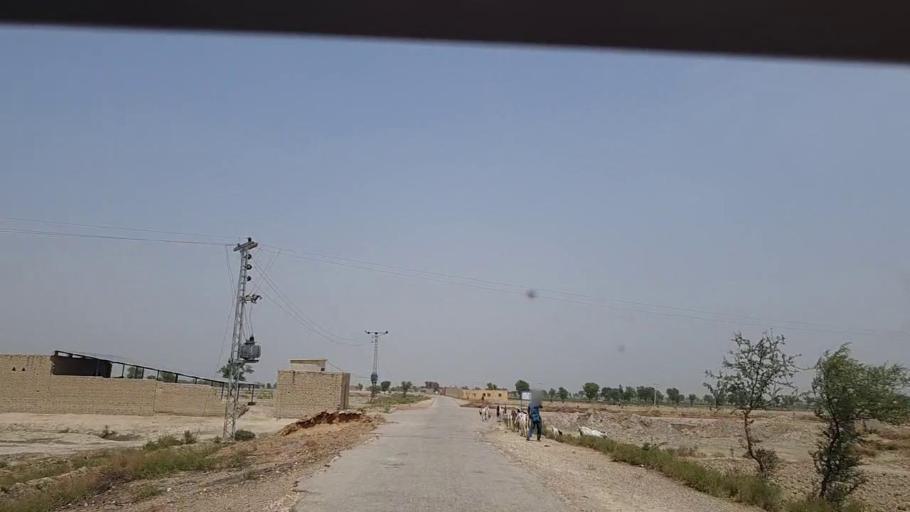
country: PK
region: Sindh
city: Khairpur Nathan Shah
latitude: 27.0213
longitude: 67.5823
